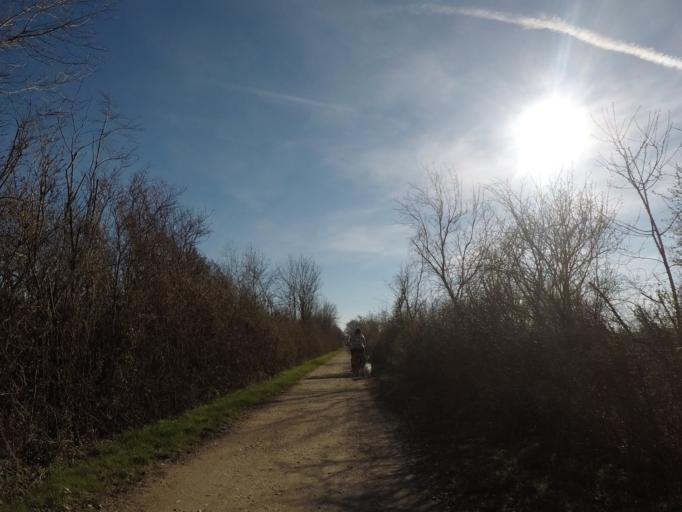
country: AT
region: Lower Austria
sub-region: Politischer Bezirk Modling
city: Vosendorf
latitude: 48.1149
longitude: 16.3472
